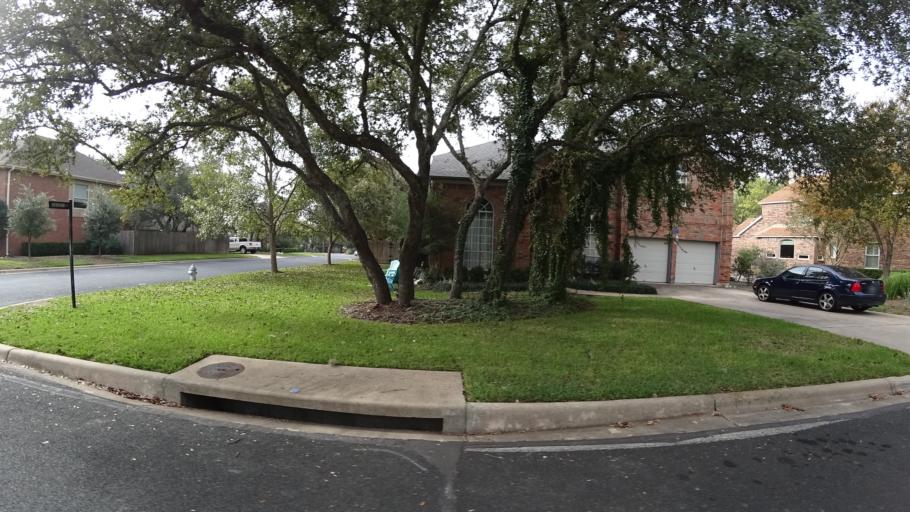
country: US
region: Texas
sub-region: Travis County
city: Shady Hollow
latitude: 30.1947
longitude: -97.8869
